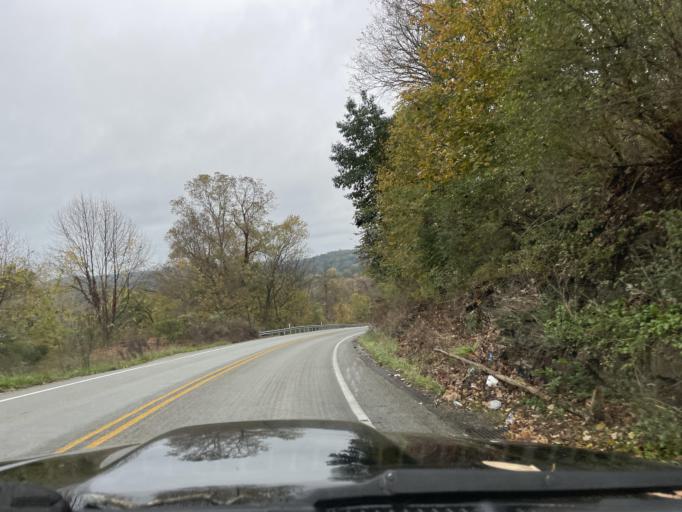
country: US
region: Pennsylvania
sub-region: Allegheny County
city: Springdale
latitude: 40.5337
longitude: -79.7676
